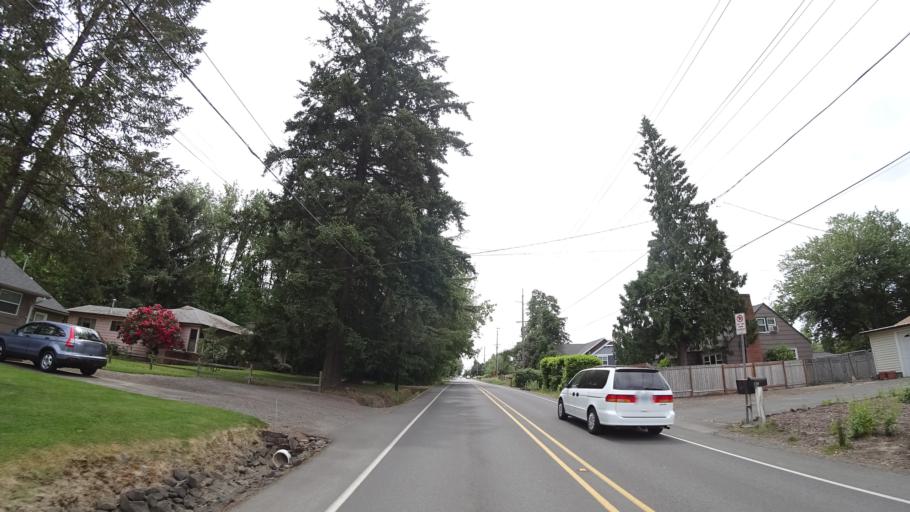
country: US
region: Oregon
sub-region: Washington County
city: Metzger
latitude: 45.4487
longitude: -122.7590
